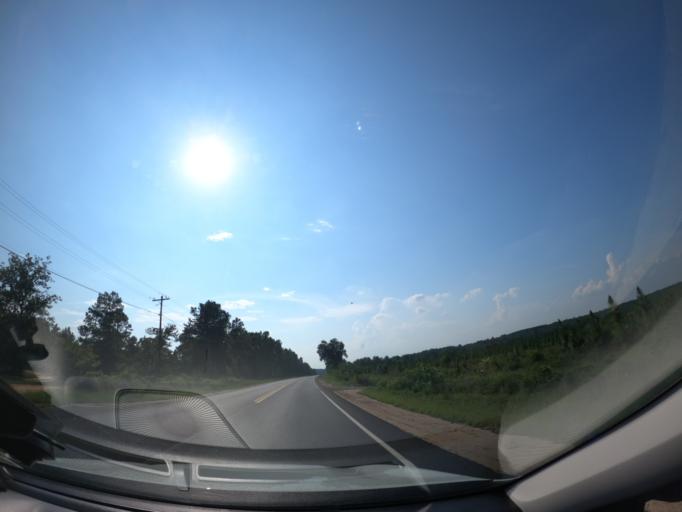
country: US
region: South Carolina
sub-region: Aiken County
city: New Ellenton
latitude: 33.3941
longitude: -81.7374
